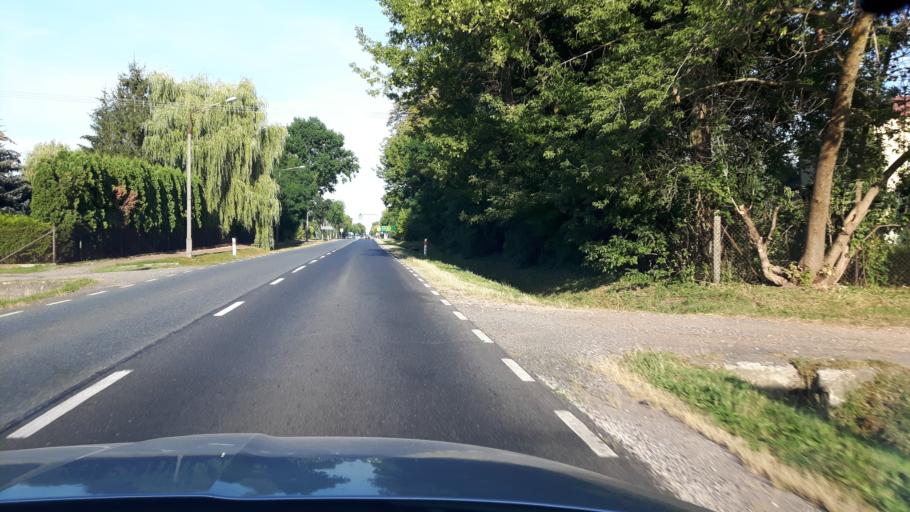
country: PL
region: Masovian Voivodeship
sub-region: Powiat legionowski
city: Wieliszew
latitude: 52.5057
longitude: 21.0021
